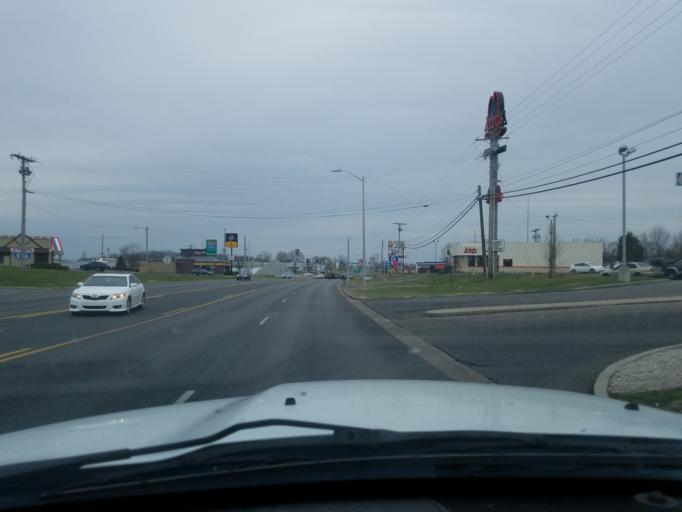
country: US
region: Indiana
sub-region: Scott County
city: Scottsburg
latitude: 38.6852
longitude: -85.7919
